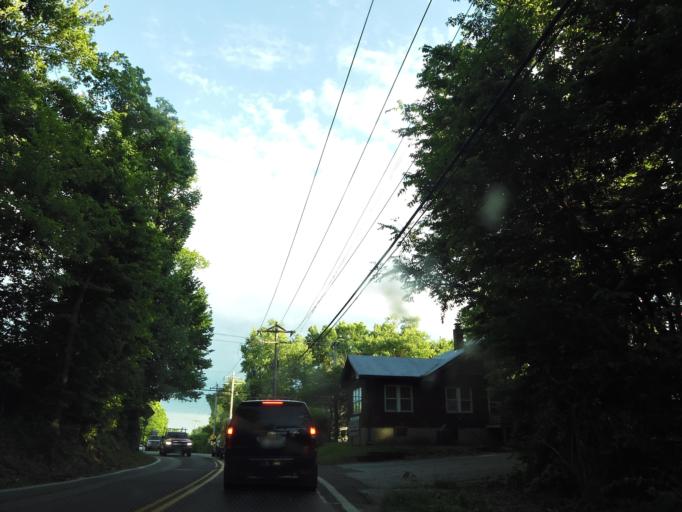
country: US
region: Missouri
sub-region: Saint Louis County
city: Wildwood
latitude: 38.6438
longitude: -90.6715
